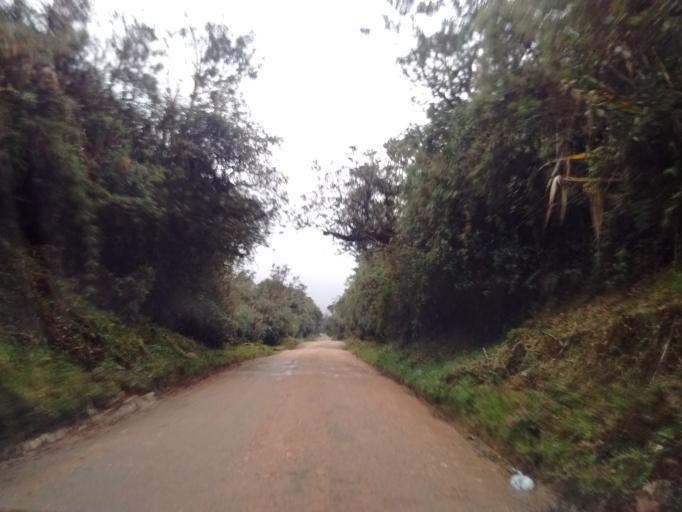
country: CO
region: Huila
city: Isnos
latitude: 2.1185
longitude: -76.3763
